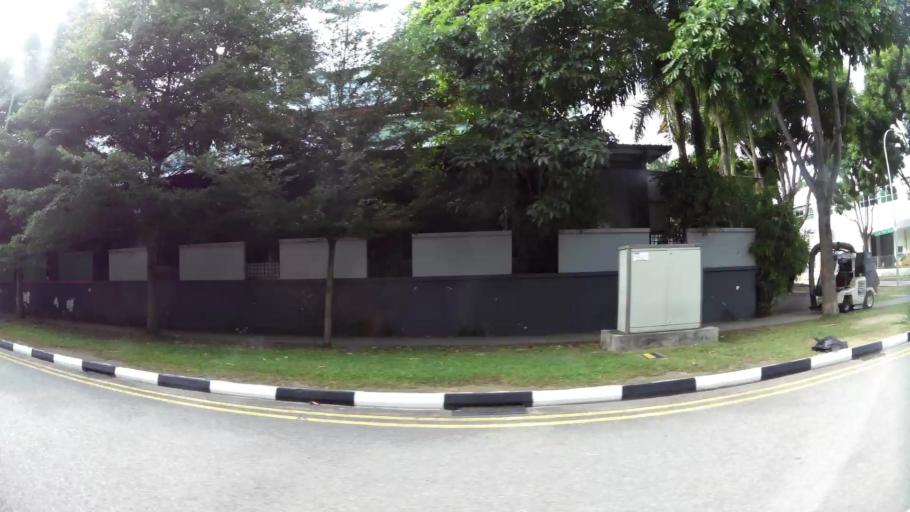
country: MY
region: Johor
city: Johor Bahru
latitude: 1.3121
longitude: 103.6297
